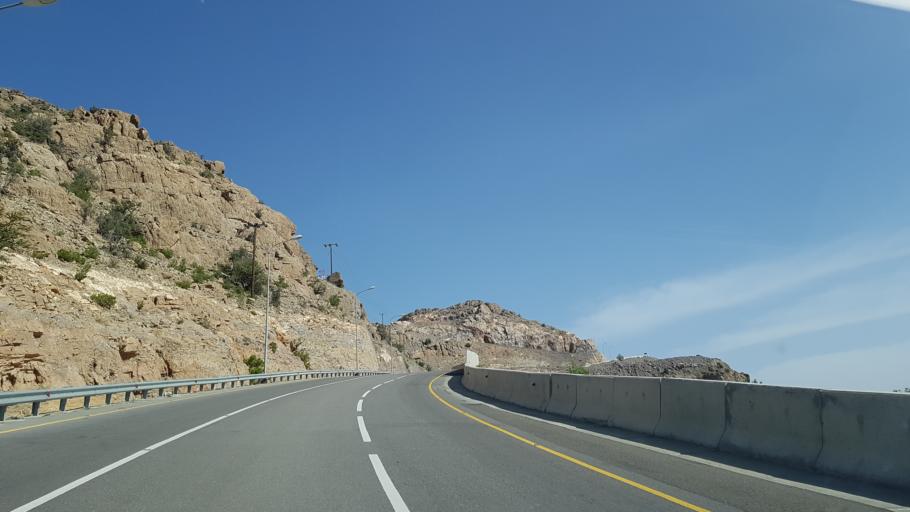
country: OM
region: Muhafazat ad Dakhiliyah
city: Izki
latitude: 23.0646
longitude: 57.7255
